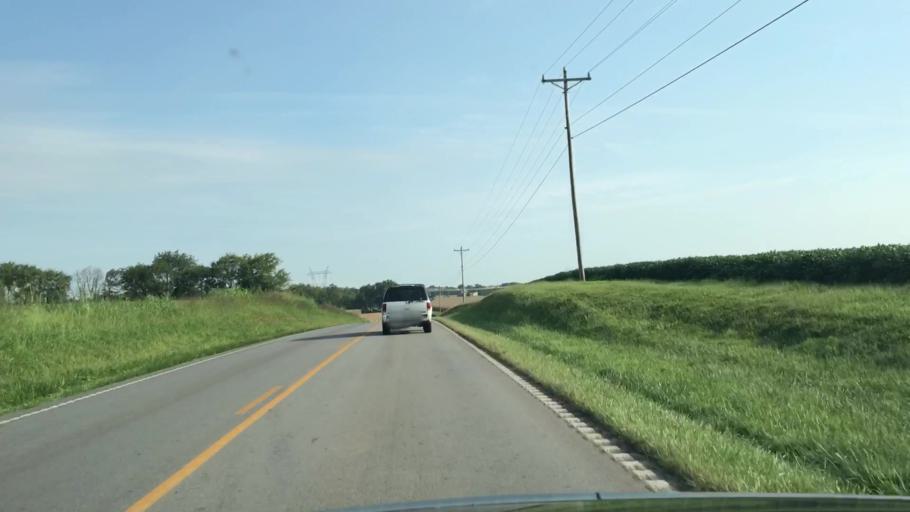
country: US
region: Kentucky
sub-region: Todd County
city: Guthrie
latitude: 36.6619
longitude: -87.1988
